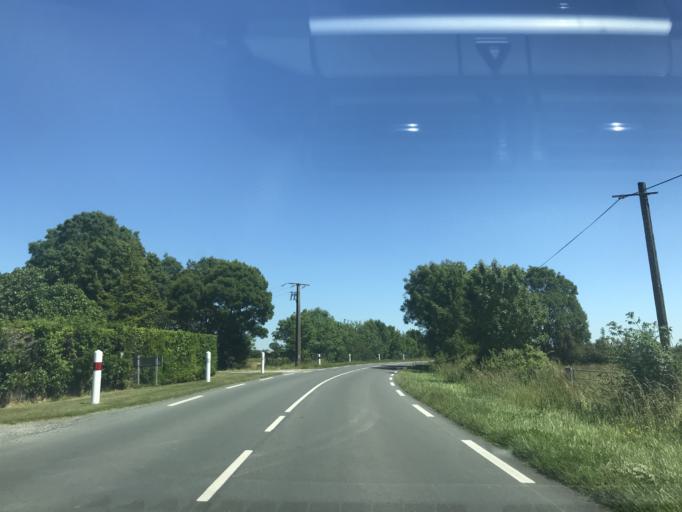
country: FR
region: Poitou-Charentes
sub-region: Departement de la Charente-Maritime
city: Meschers-sur-Gironde
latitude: 45.5620
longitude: -0.9373
